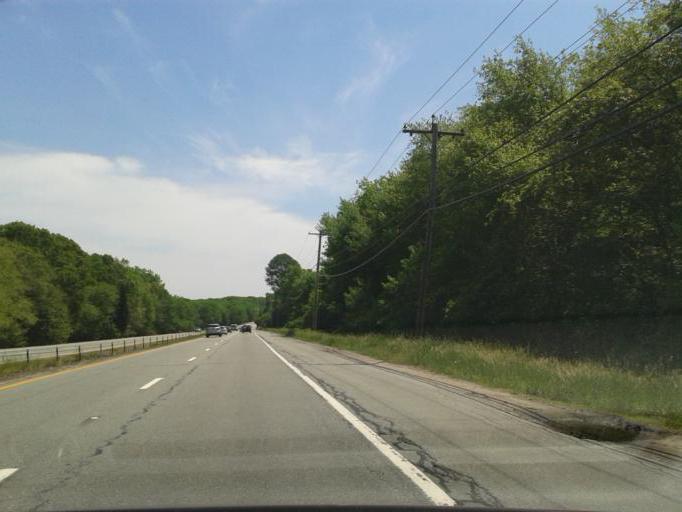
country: US
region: Rhode Island
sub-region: Washington County
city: North Kingstown
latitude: 41.5104
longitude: -71.4604
